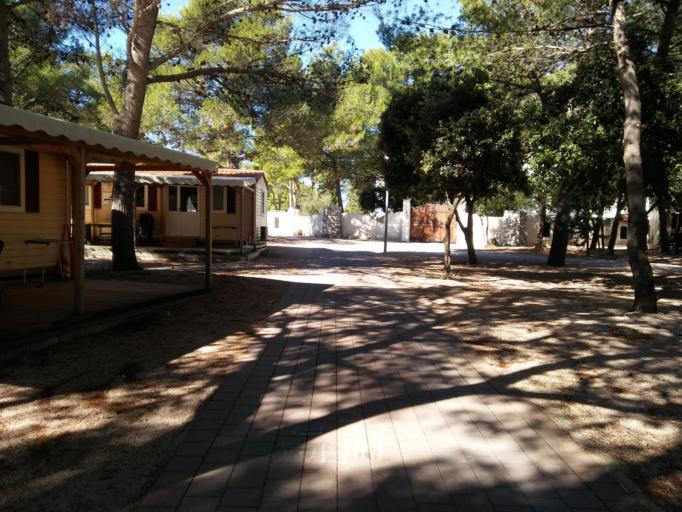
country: HR
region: Sibensko-Kniniska
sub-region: Grad Sibenik
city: Brodarica
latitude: 43.6965
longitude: 15.8903
